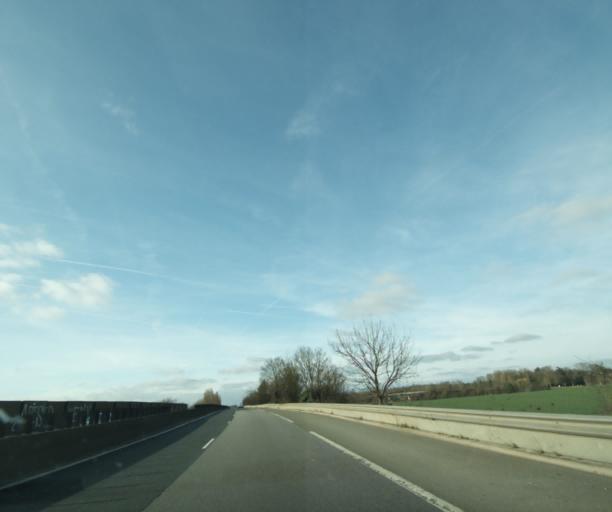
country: FR
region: Ile-de-France
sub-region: Departement des Yvelines
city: Rambouillet
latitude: 48.6513
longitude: 1.8438
